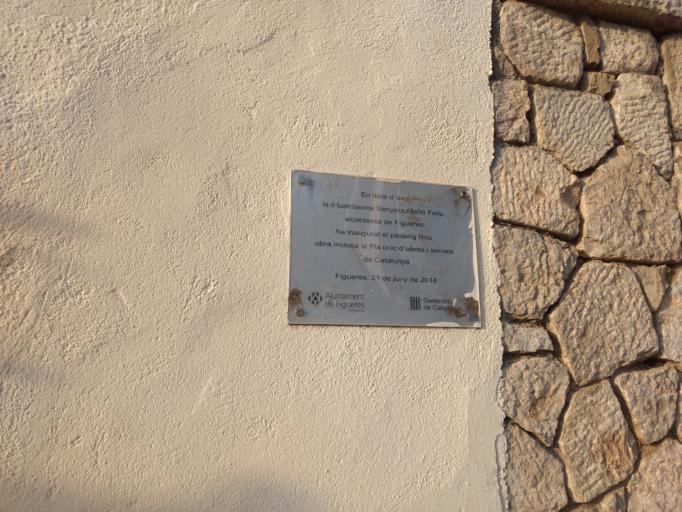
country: ES
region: Catalonia
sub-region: Provincia de Girona
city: Figueres
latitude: 42.2665
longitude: 2.9564
